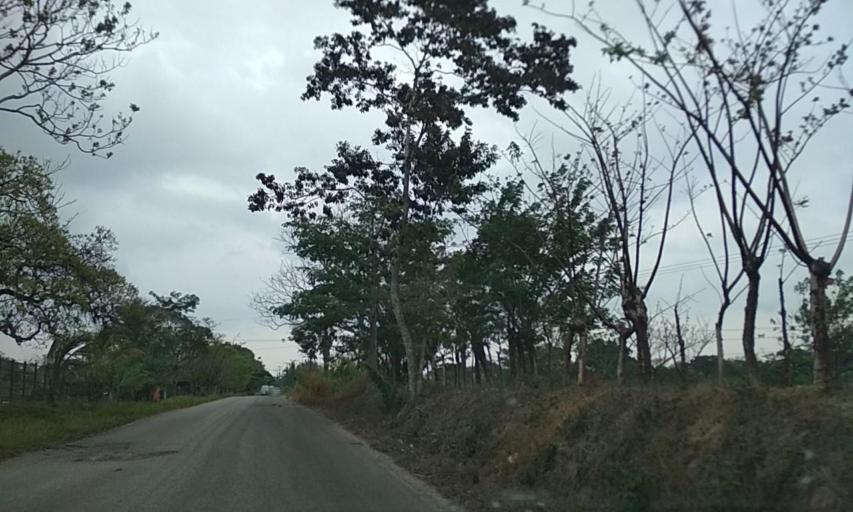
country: MX
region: Veracruz
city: Las Choapas
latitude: 17.7448
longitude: -94.1105
